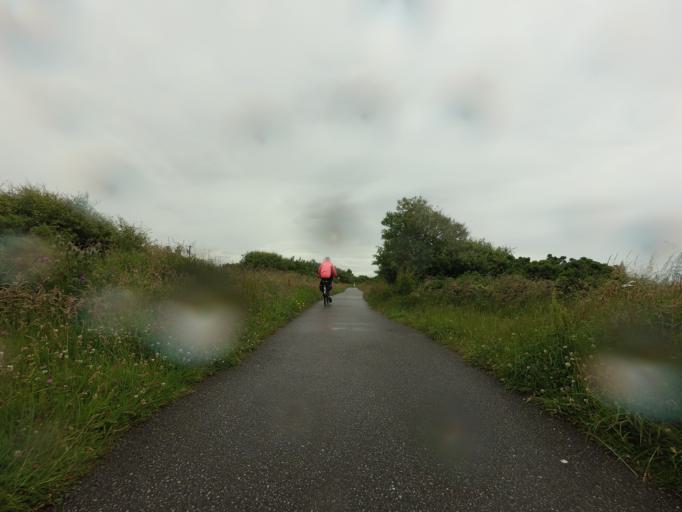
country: GB
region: Scotland
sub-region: Moray
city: Findochty
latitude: 57.6867
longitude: -2.9271
